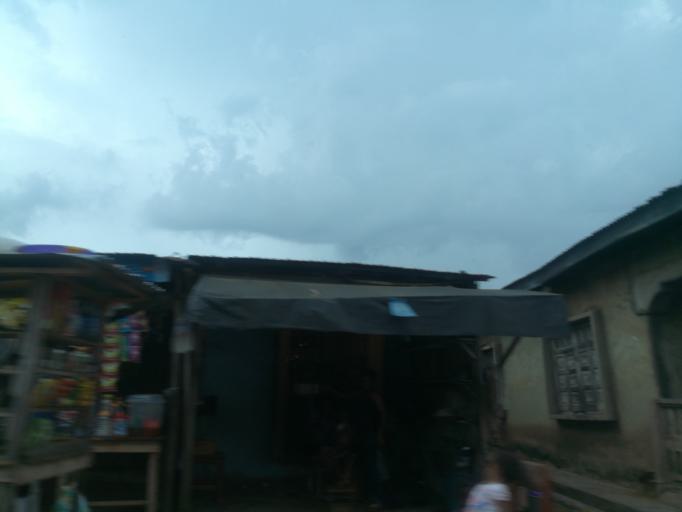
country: NG
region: Oyo
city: Moniya
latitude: 7.4652
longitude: 3.9114
